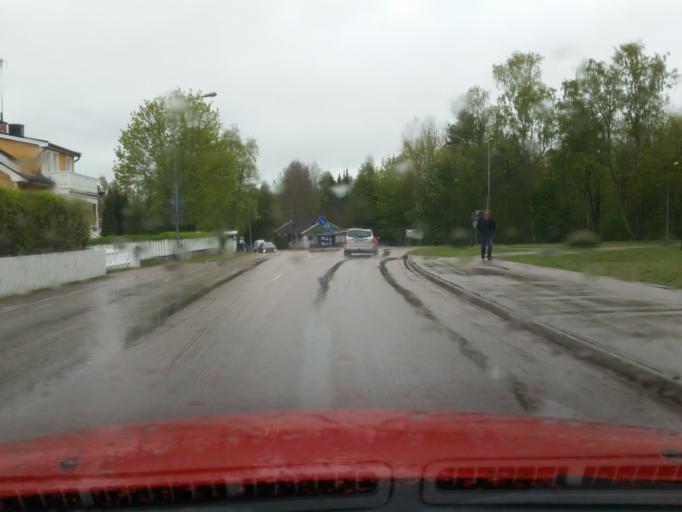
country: SE
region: Dalarna
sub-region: Hedemora Kommun
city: Hedemora
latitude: 60.2878
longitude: 15.9749
